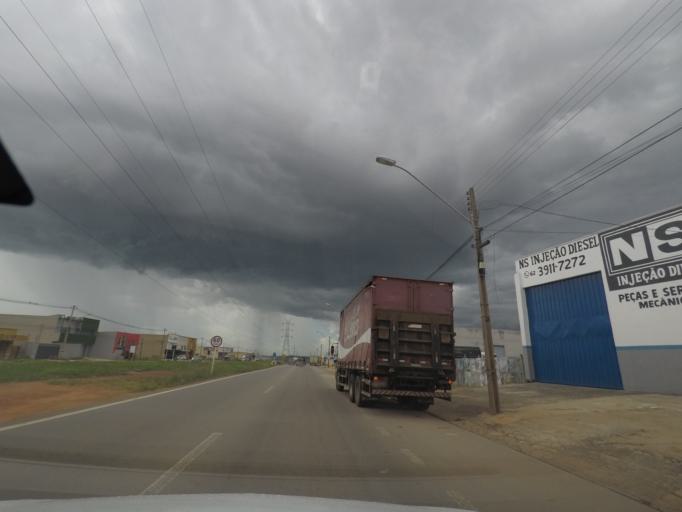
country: BR
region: Goias
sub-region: Goiania
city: Goiania
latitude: -16.7377
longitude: -49.3465
